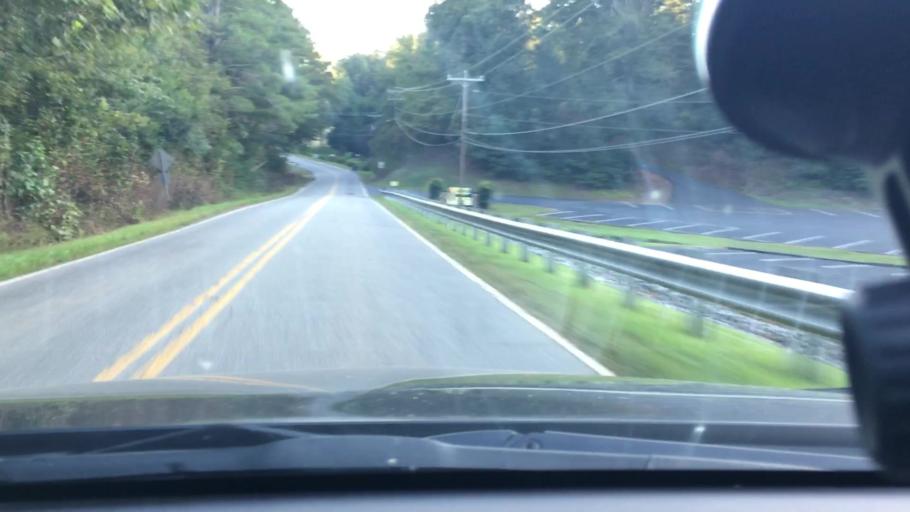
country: US
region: North Carolina
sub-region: Polk County
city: Columbus
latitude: 35.2720
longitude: -82.1829
